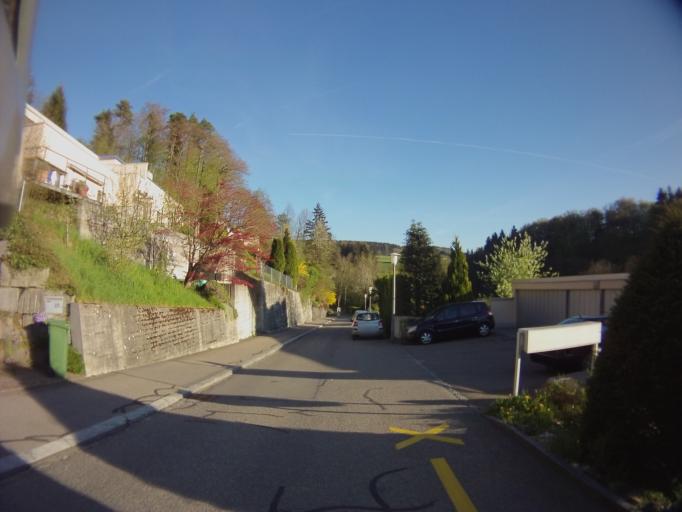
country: CH
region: Zurich
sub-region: Bezirk Dietikon
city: Birmensdorf
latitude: 47.3482
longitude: 8.4450
